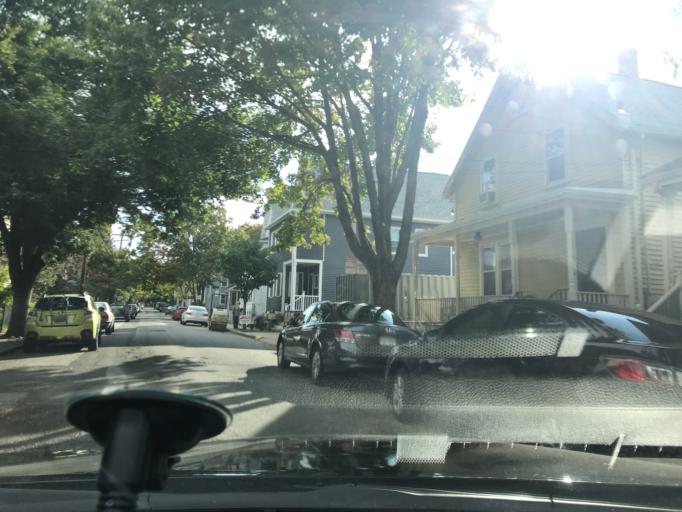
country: US
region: Massachusetts
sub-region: Middlesex County
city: Arlington
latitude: 42.3958
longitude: -71.1342
